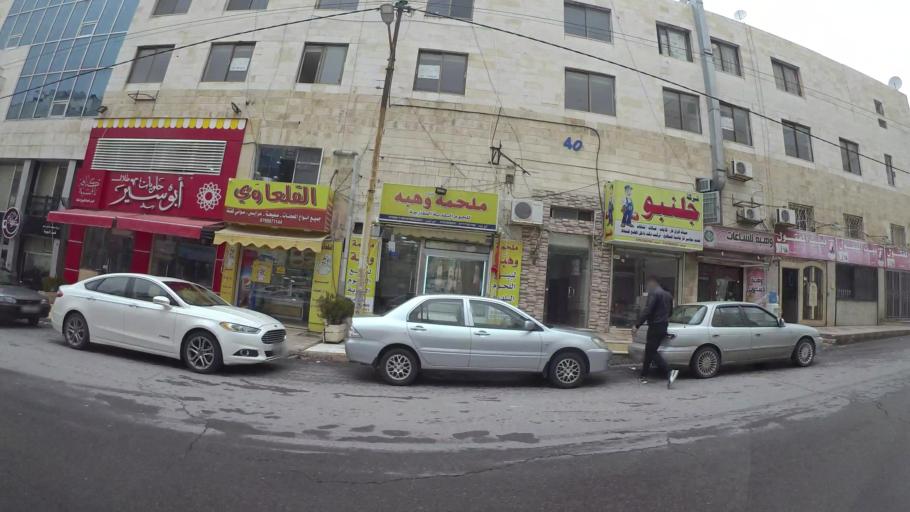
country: JO
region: Amman
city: Wadi as Sir
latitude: 31.9580
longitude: 35.8633
